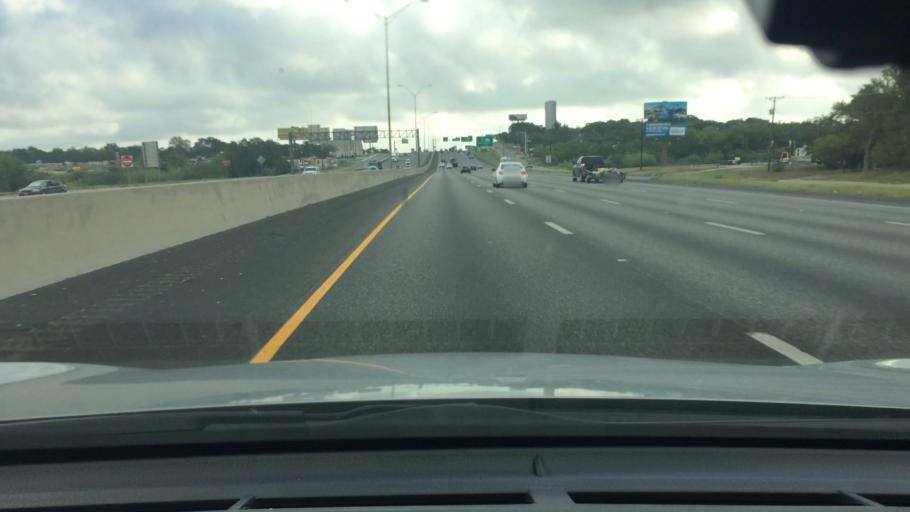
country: US
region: Texas
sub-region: Comal County
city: New Braunfels
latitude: 29.6747
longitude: -98.1521
